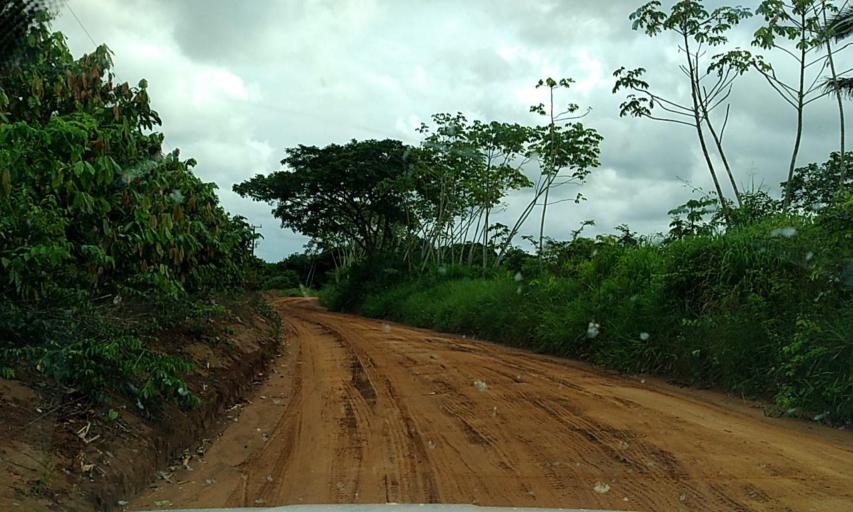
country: BR
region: Para
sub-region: Altamira
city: Altamira
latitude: -3.3046
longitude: -52.6877
